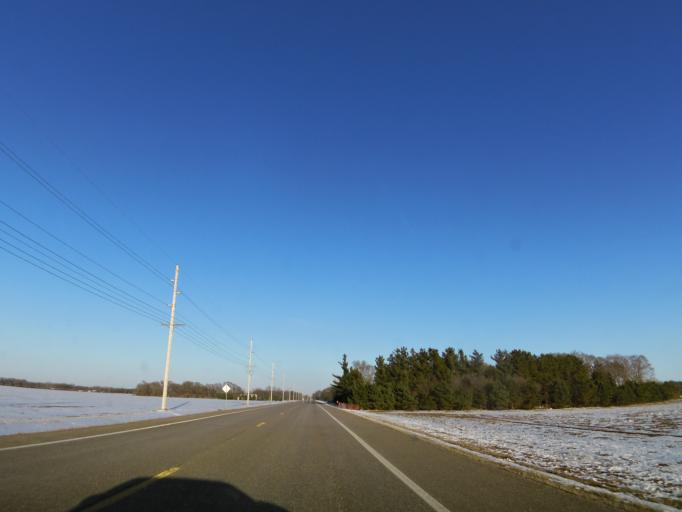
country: US
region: Minnesota
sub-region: Dakota County
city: Hastings
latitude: 44.6733
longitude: -92.8711
